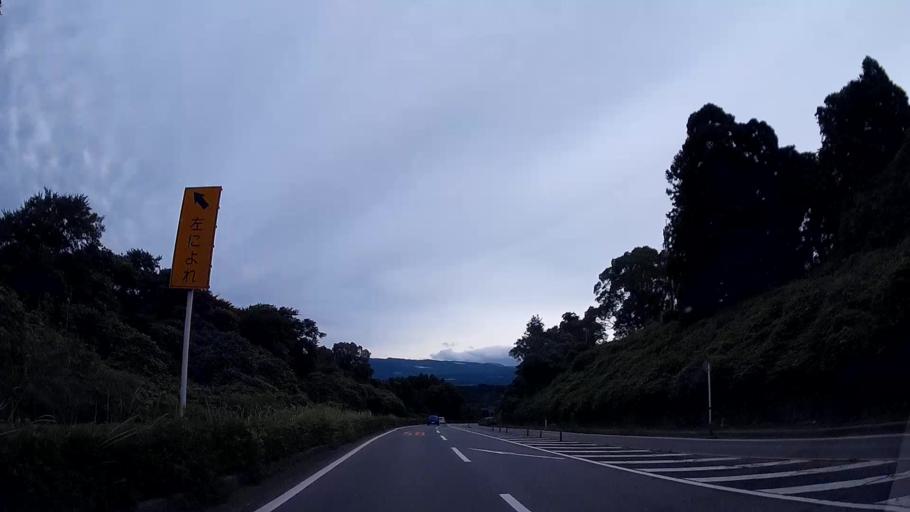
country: JP
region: Kumamoto
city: Ozu
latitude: 32.8427
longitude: 130.8534
